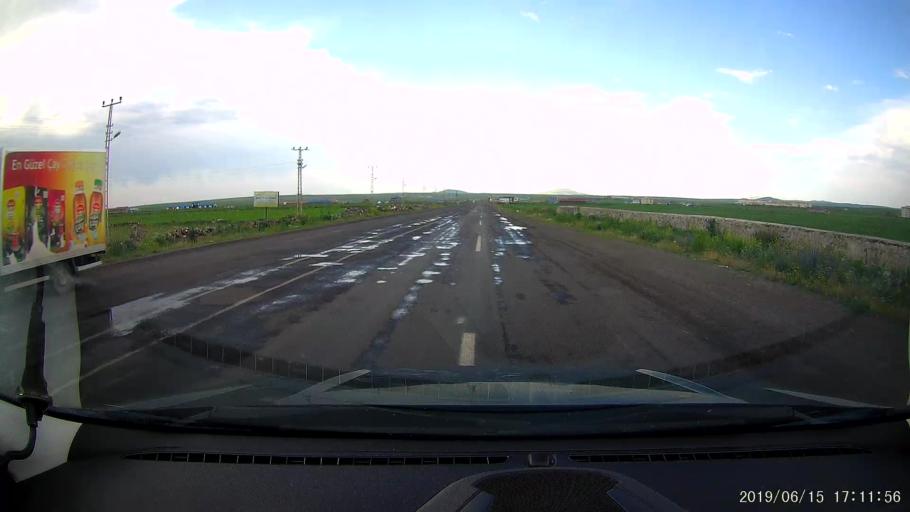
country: TR
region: Kars
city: Kars
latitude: 40.6142
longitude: 43.1394
